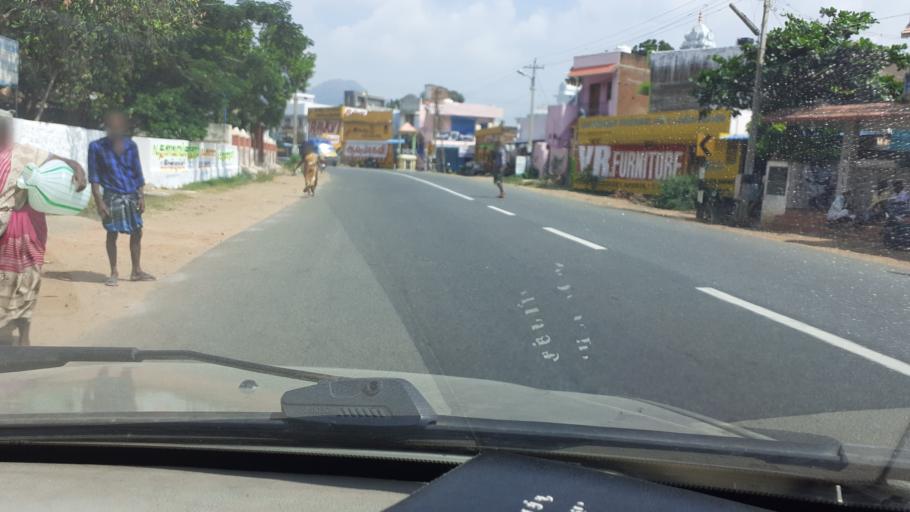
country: IN
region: Tamil Nadu
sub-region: Kanniyakumari
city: Suchindram
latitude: 8.2470
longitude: 77.5205
